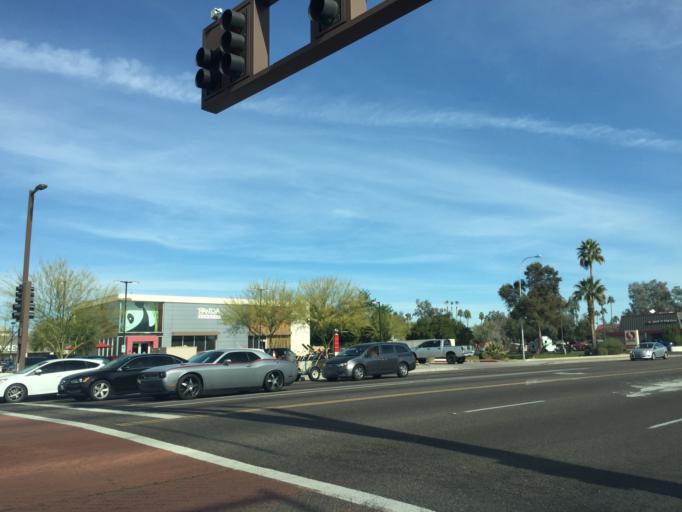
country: US
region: Arizona
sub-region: Maricopa County
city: Tempe
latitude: 33.4074
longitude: -111.9261
